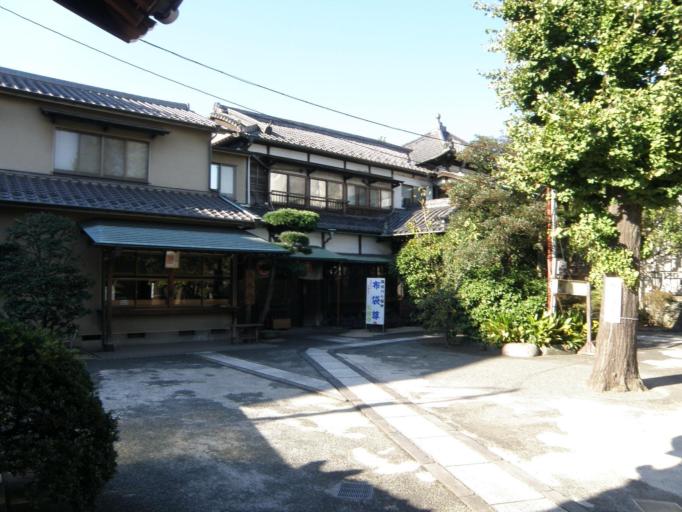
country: JP
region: Tokyo
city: Urayasu
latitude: 35.7172
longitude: 139.8090
